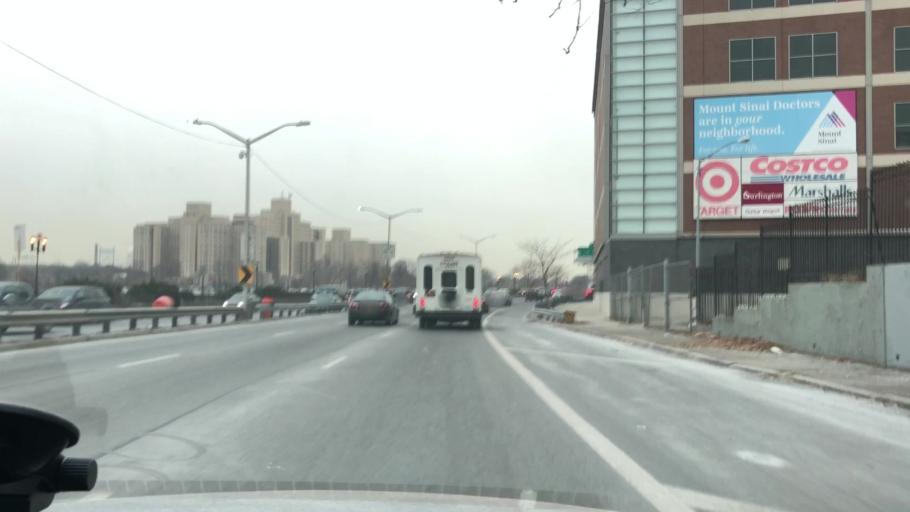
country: US
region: New York
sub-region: New York County
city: Manhattan
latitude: 40.7964
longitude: -73.9295
